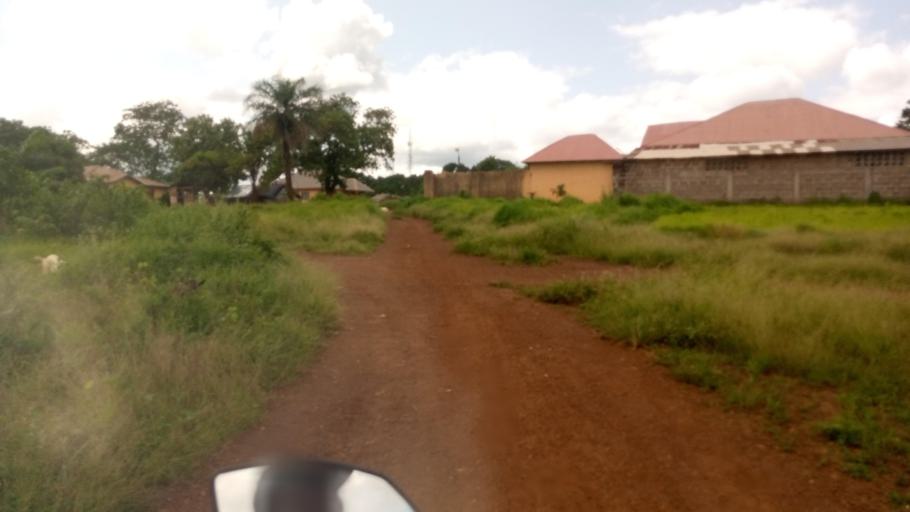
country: SL
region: Northern Province
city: Kamakwie
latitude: 9.4923
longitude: -12.2349
